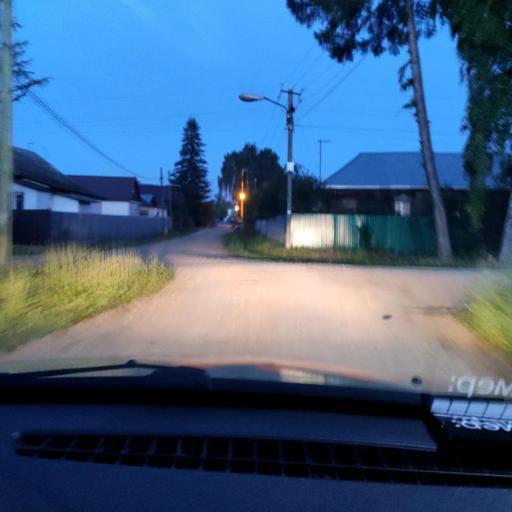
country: RU
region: Bashkortostan
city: Iglino
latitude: 54.8358
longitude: 56.4104
